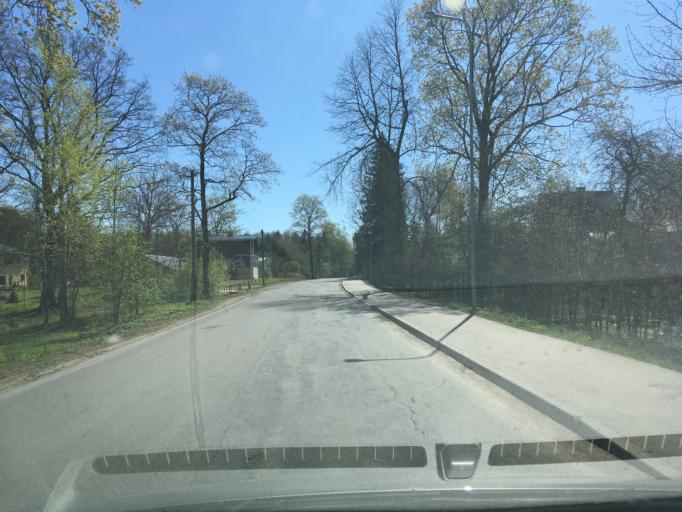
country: EE
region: Harju
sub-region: Raasiku vald
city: Arukula
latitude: 59.3671
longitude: 25.0810
